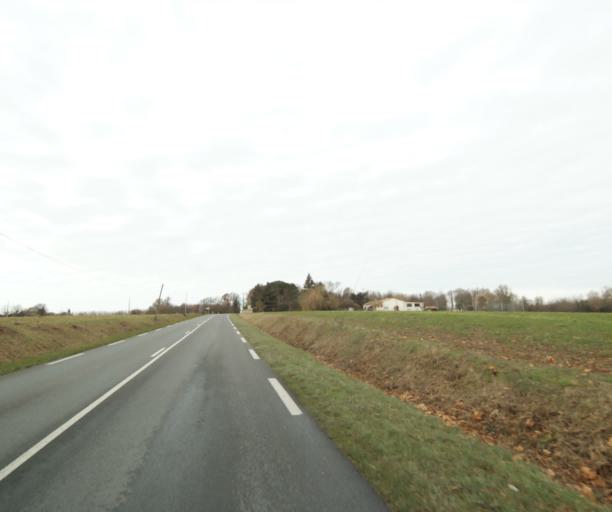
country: FR
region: Poitou-Charentes
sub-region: Departement de la Charente-Maritime
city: Corme-Royal
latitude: 45.7353
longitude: -0.7772
